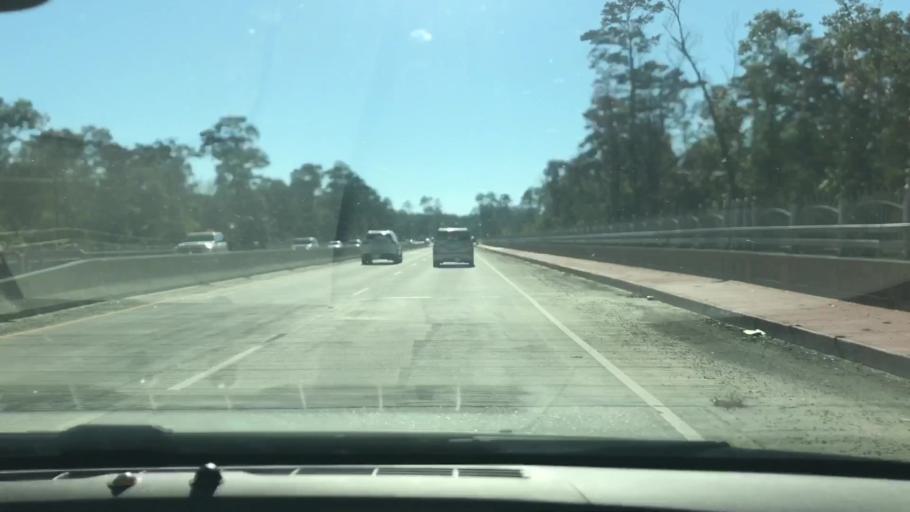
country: US
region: Louisiana
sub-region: Saint Tammany Parish
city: Covington
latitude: 30.4649
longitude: -90.1172
